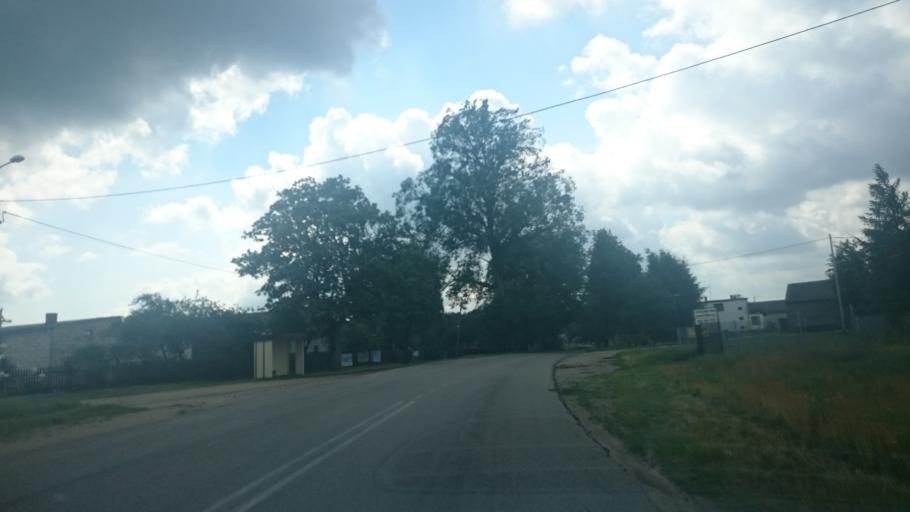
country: PL
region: Pomeranian Voivodeship
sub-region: Powiat koscierski
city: Stara Kiszewa
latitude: 53.9782
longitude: 18.2275
